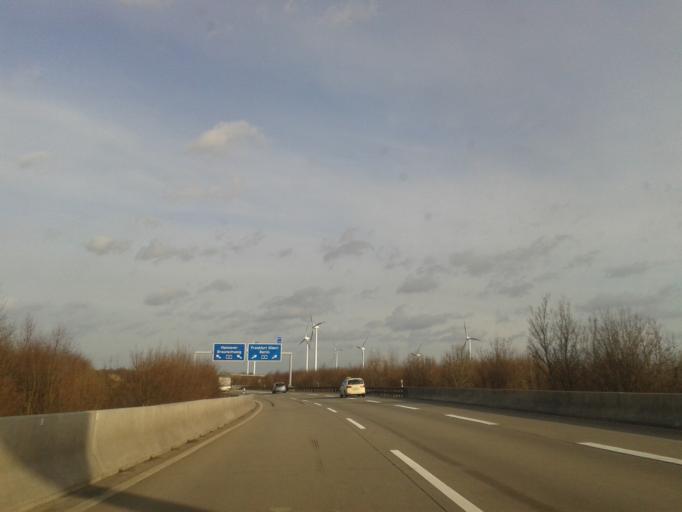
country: DE
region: Saxony-Anhalt
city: Dahlenwarsleben
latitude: 52.1631
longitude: 11.5456
